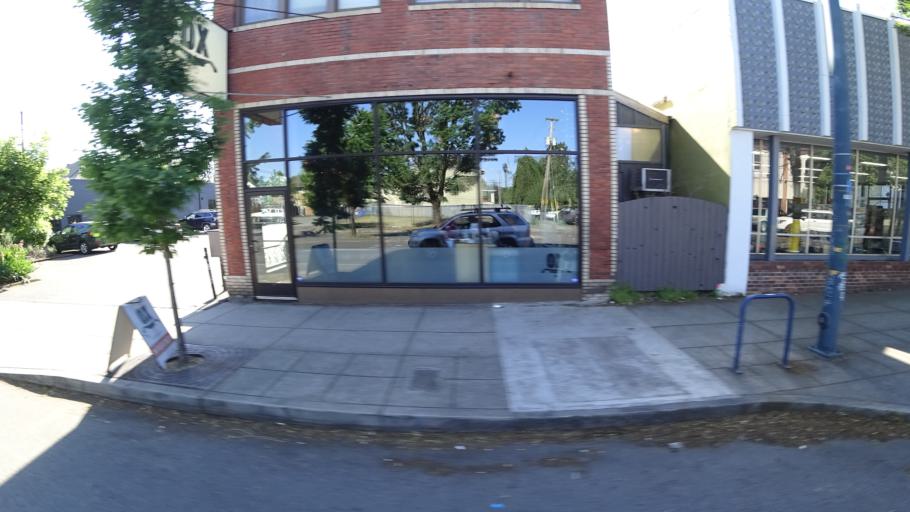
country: US
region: Oregon
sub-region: Multnomah County
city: Portland
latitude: 45.5395
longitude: -122.6617
